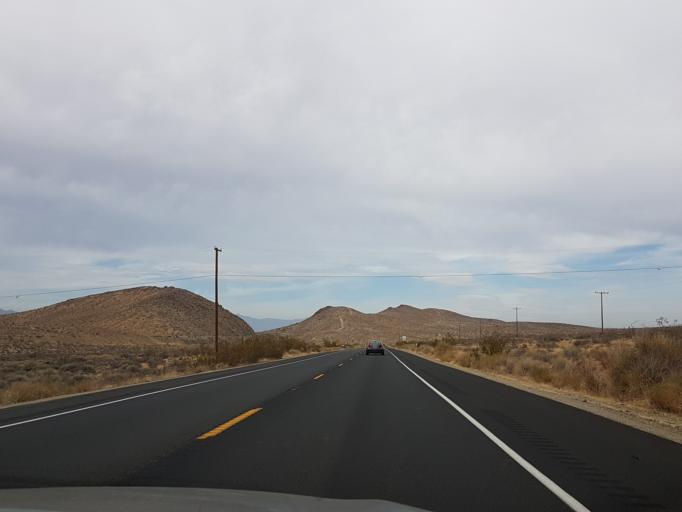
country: US
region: California
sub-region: Kern County
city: Ridgecrest
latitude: 35.5378
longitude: -117.6850
